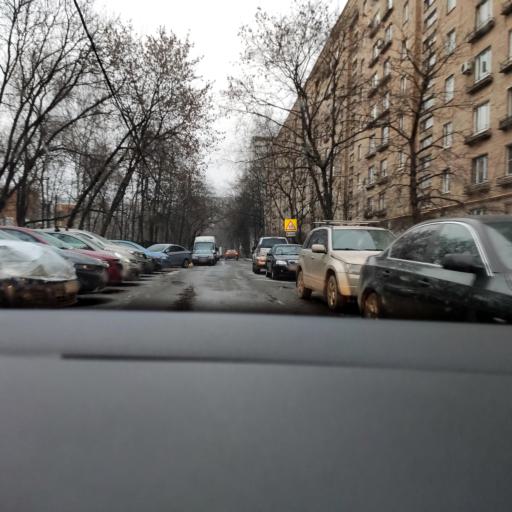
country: RU
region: Moscow
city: Sviblovo
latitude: 55.8477
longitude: 37.6413
